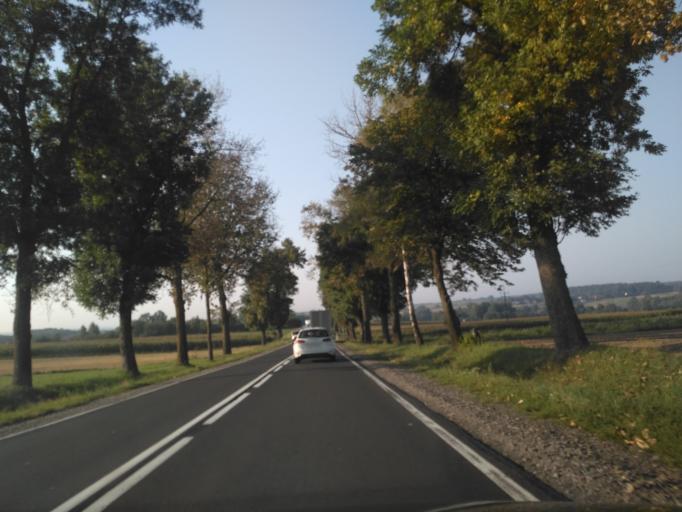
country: PL
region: Lublin Voivodeship
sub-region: Powiat krasnicki
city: Szastarka
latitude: 50.8091
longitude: 22.3196
